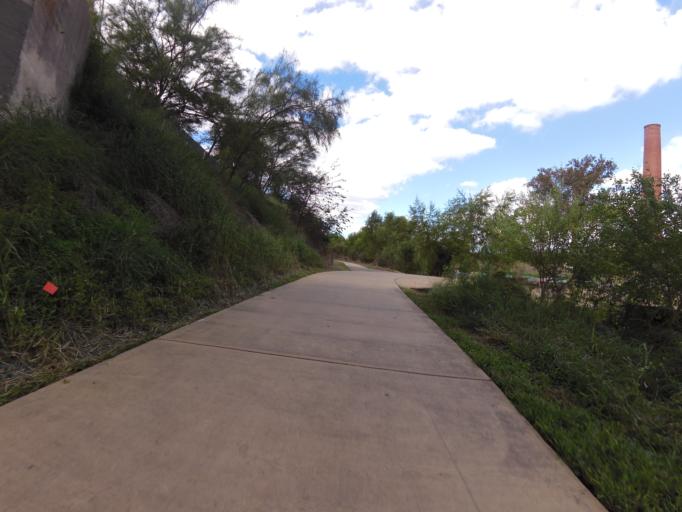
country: US
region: Texas
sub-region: Bexar County
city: San Antonio
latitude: 29.3974
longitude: -98.4904
